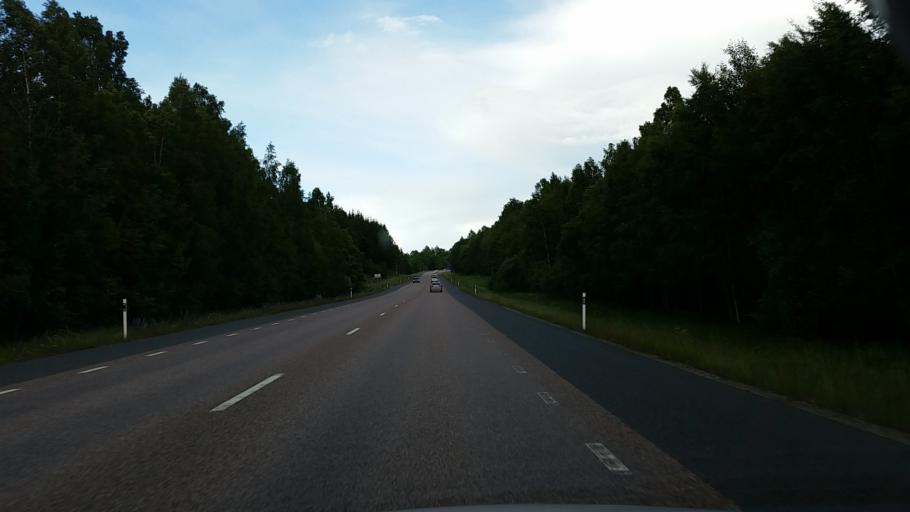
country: SE
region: Vaestmanland
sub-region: Fagersta Kommun
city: Fagersta
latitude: 59.9652
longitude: 15.7496
